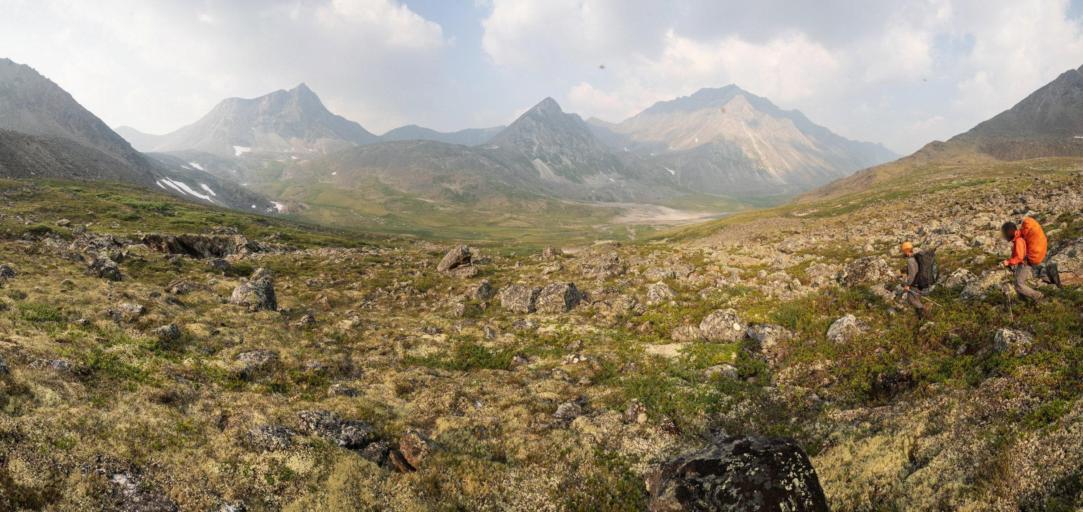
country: RU
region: Transbaikal Territory
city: Chara
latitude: 56.8182
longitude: 117.1323
